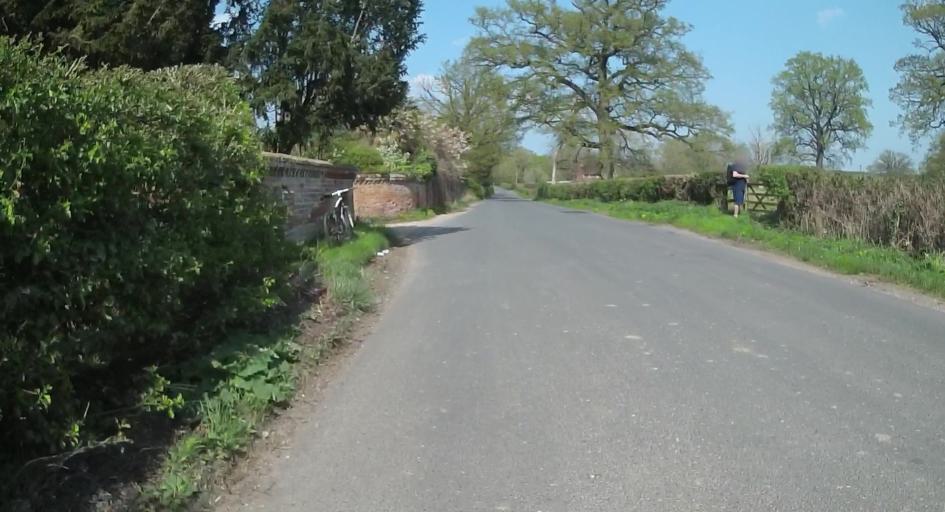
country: GB
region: England
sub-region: Hampshire
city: Basingstoke
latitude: 51.3070
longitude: -1.0866
